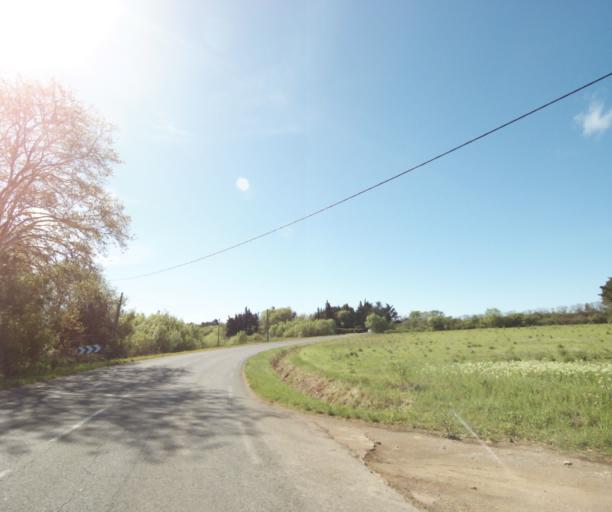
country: FR
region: Languedoc-Roussillon
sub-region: Departement de l'Herault
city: Villeneuve-les-Maguelone
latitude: 43.5457
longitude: 3.8479
